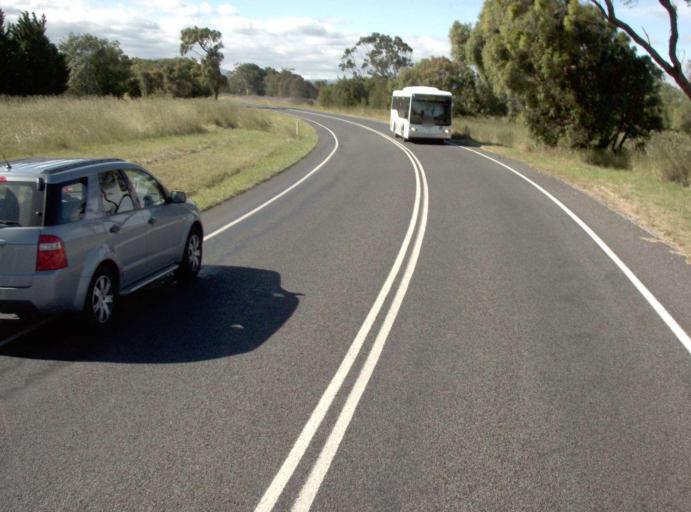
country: AU
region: Victoria
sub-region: Latrobe
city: Traralgon
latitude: -38.1656
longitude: 146.4894
